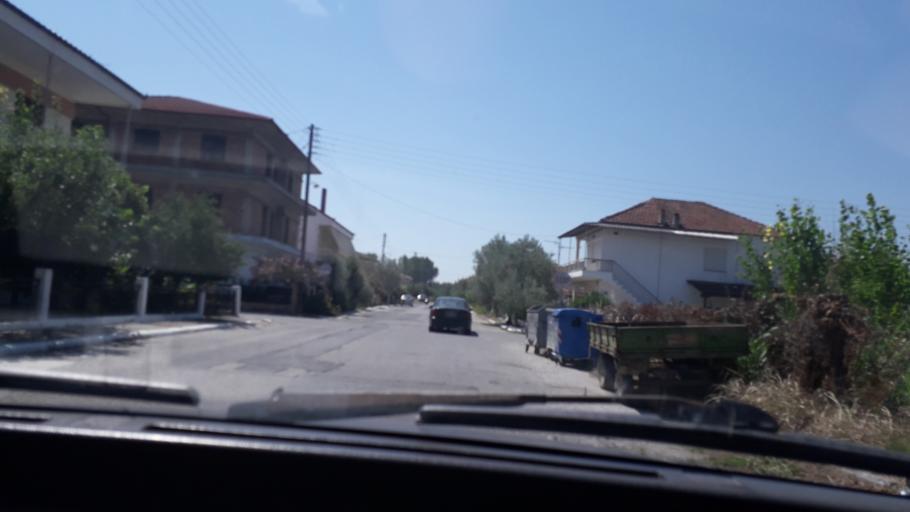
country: GR
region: Central Macedonia
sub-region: Nomos Pellis
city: Aridaia
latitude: 40.9690
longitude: 22.0591
